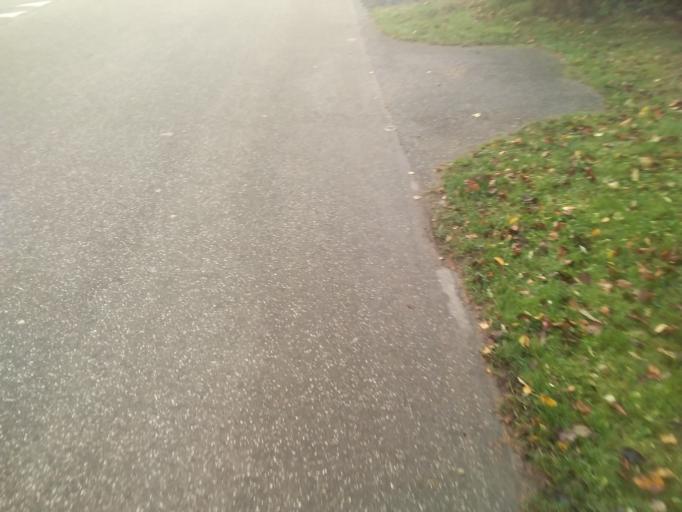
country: DK
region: Capital Region
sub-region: Herlev Kommune
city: Herlev
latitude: 55.7488
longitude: 12.4118
